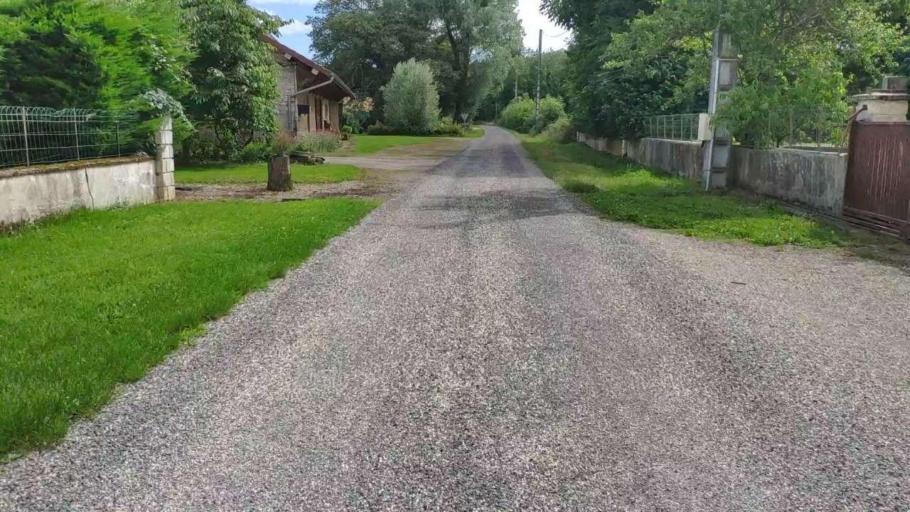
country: FR
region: Franche-Comte
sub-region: Departement du Jura
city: Bletterans
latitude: 46.8165
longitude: 5.4287
